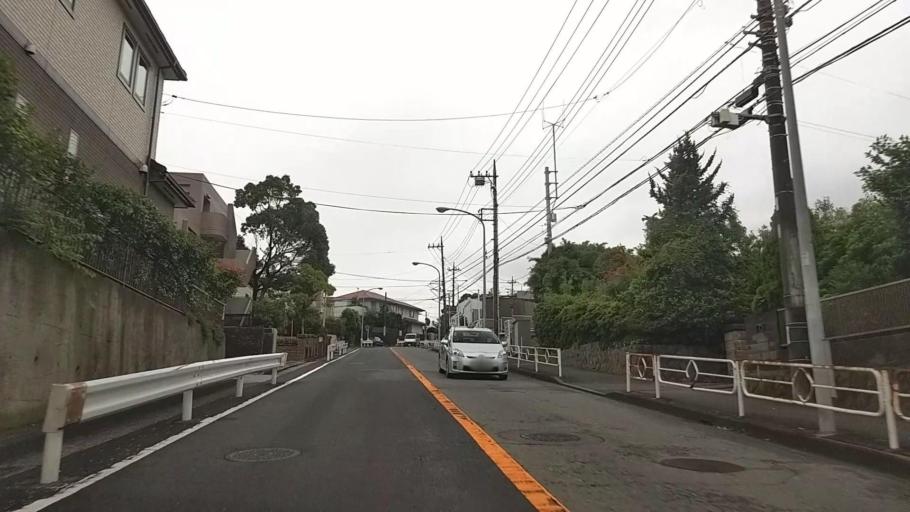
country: JP
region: Kanagawa
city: Yokohama
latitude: 35.3902
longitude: 139.5796
